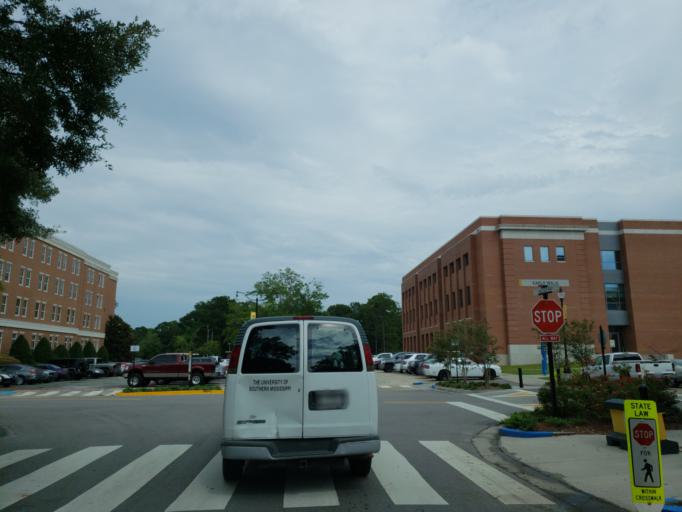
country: US
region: Mississippi
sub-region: Forrest County
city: Hattiesburg
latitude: 31.3306
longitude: -89.3307
